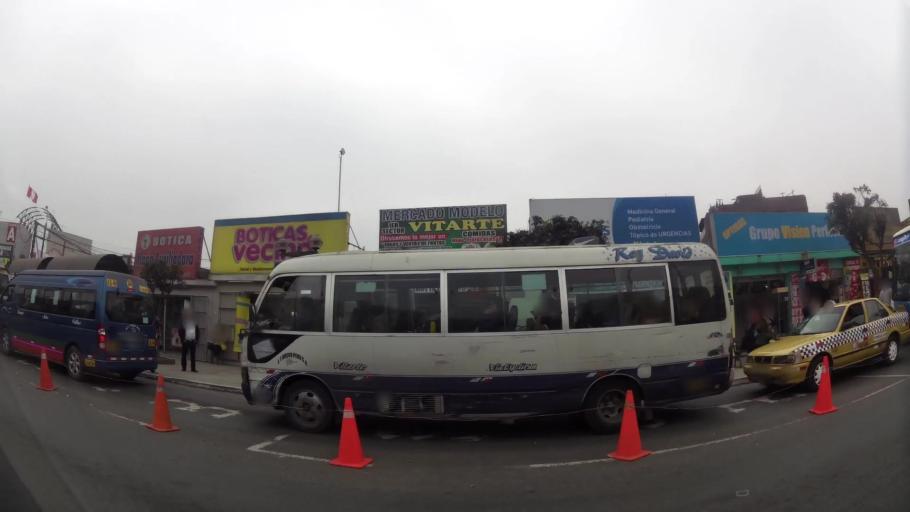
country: PE
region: Lima
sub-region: Lima
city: Vitarte
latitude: -12.0258
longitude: -76.9197
